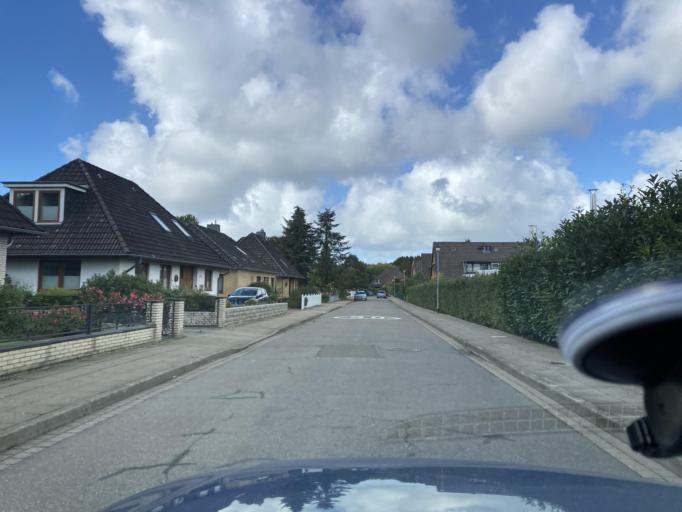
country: DE
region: Schleswig-Holstein
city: Wesseln
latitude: 54.1859
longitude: 9.0848
